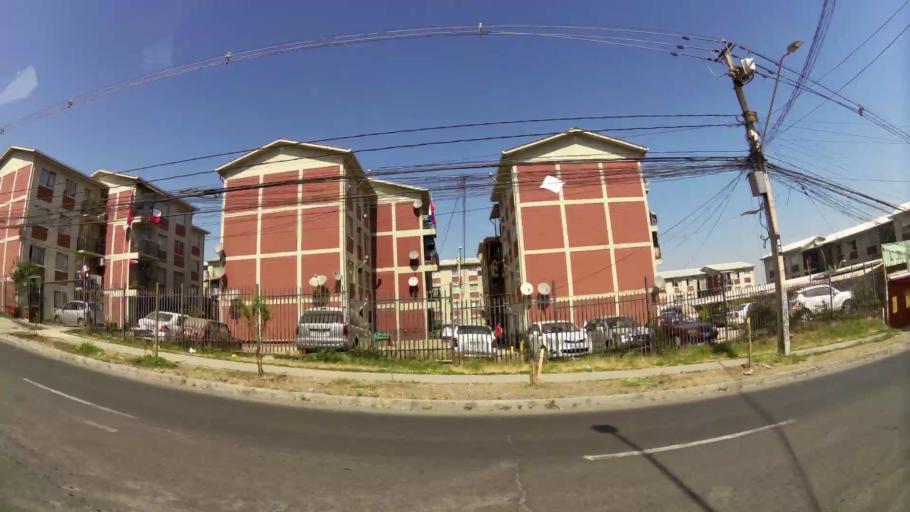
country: CL
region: Santiago Metropolitan
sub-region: Provincia de Santiago
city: Villa Presidente Frei, Nunoa, Santiago, Chile
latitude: -33.4729
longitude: -70.5356
